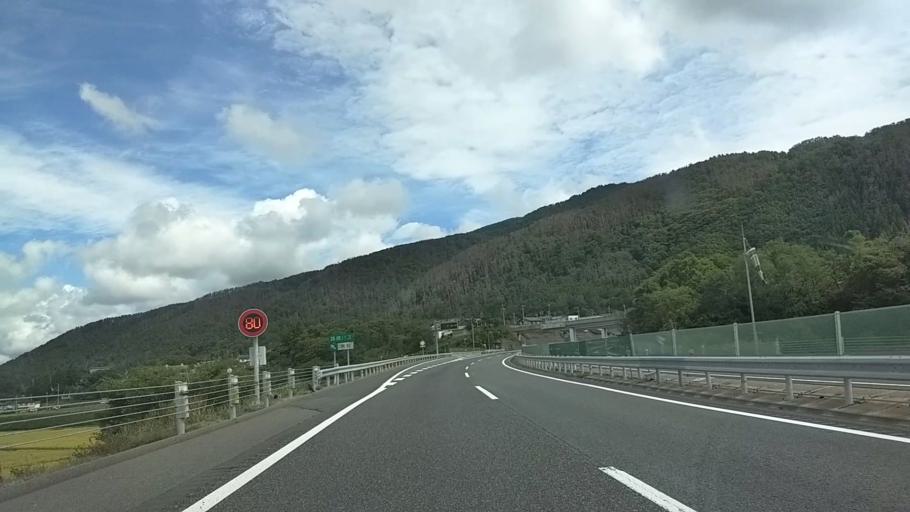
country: JP
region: Nagano
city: Toyoshina
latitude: 36.3262
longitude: 137.9245
